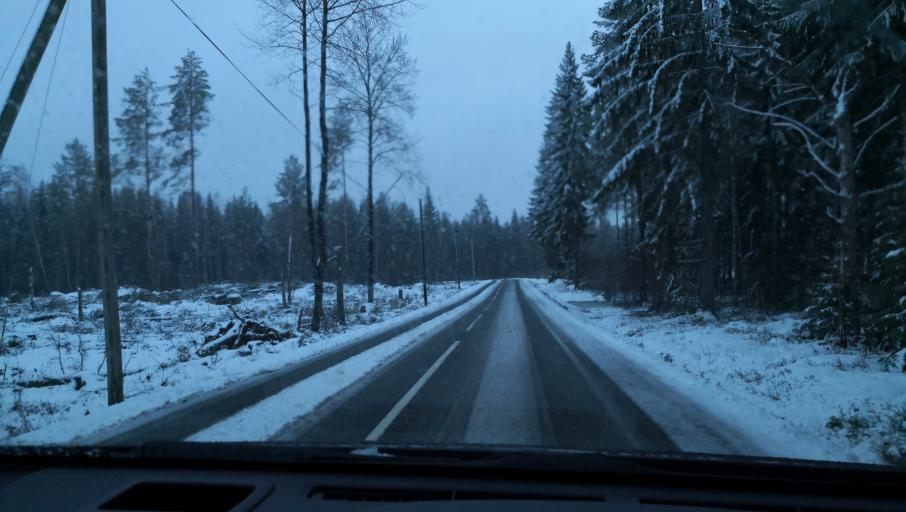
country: SE
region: Vaestmanland
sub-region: Kopings Kommun
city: Kolsva
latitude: 59.5852
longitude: 15.8048
